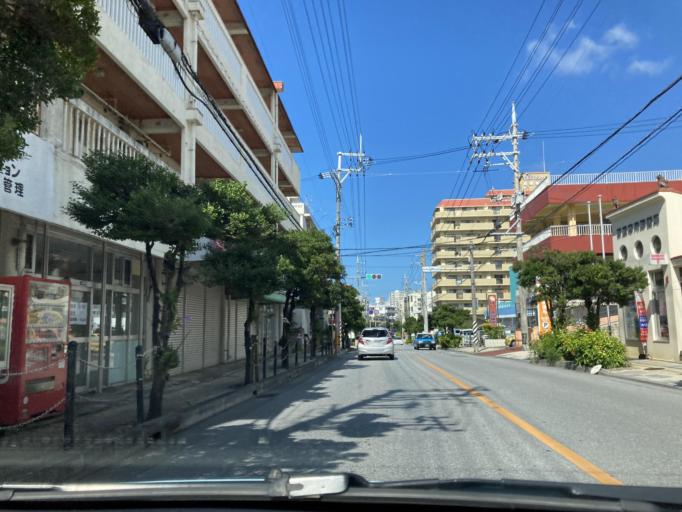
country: JP
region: Okinawa
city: Naha-shi
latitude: 26.2166
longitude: 127.7088
